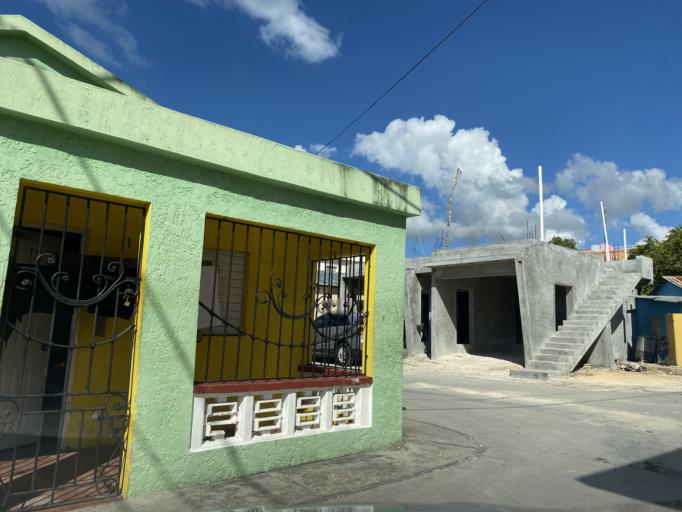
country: DO
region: La Romana
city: La Romana
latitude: 18.3672
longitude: -68.8393
